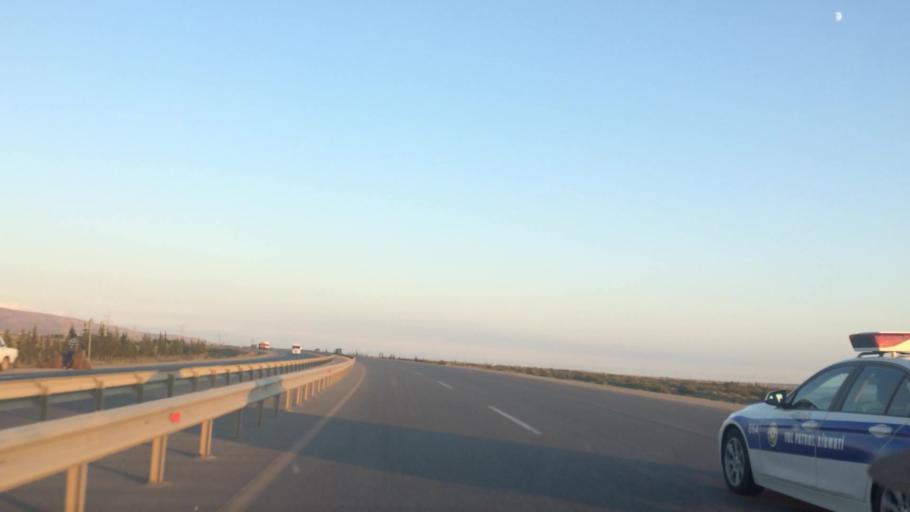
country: AZ
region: Baki
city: Qobustan
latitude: 39.9835
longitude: 49.2146
